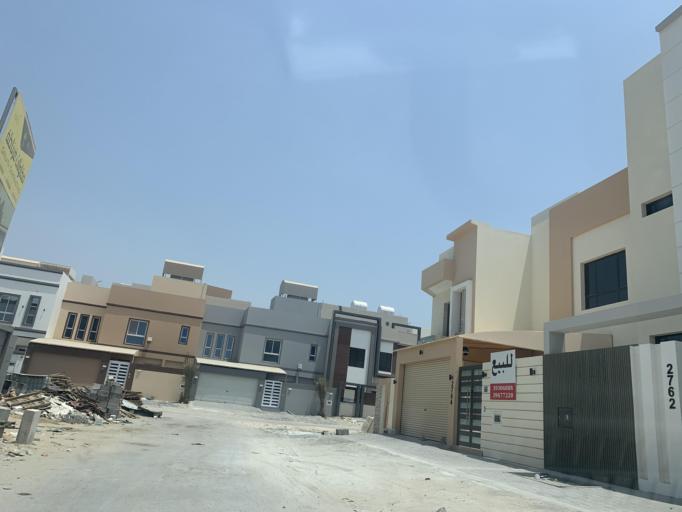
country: BH
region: Manama
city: Jidd Hafs
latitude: 26.2129
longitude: 50.4692
